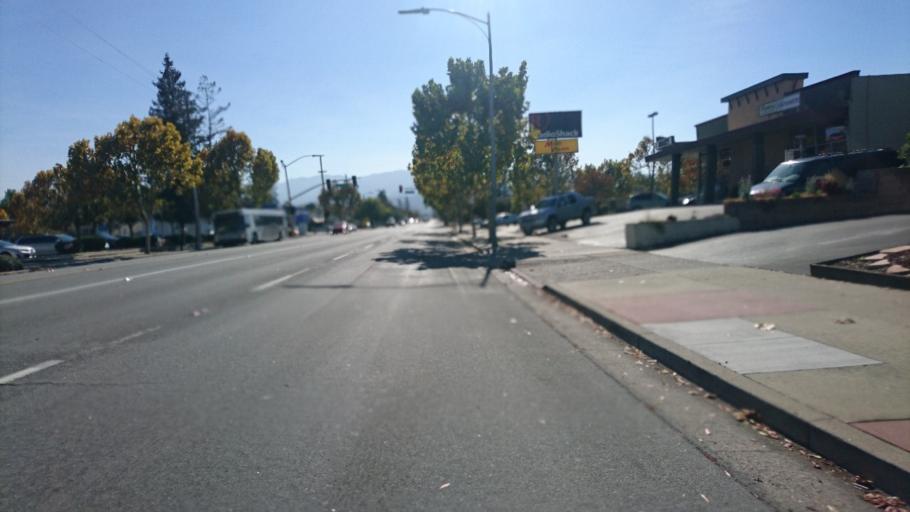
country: US
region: California
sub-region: Santa Clara County
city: Cambrian Park
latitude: 37.2682
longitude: -121.9315
